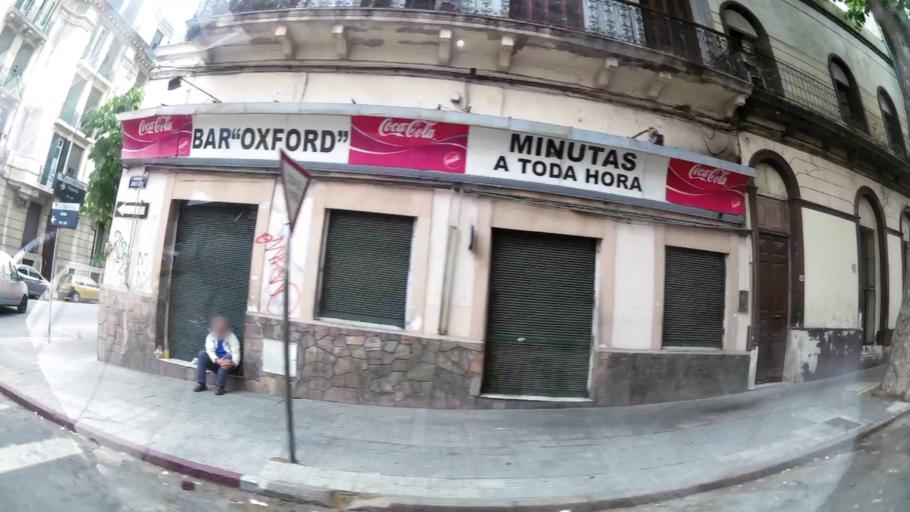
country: UY
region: Montevideo
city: Montevideo
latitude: -34.9026
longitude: -56.1984
